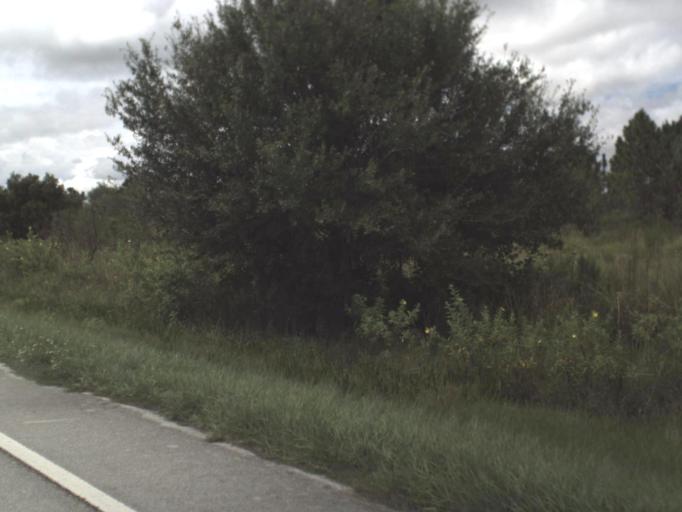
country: US
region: Florida
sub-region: Hardee County
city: Bowling Green
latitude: 27.5952
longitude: -82.0427
